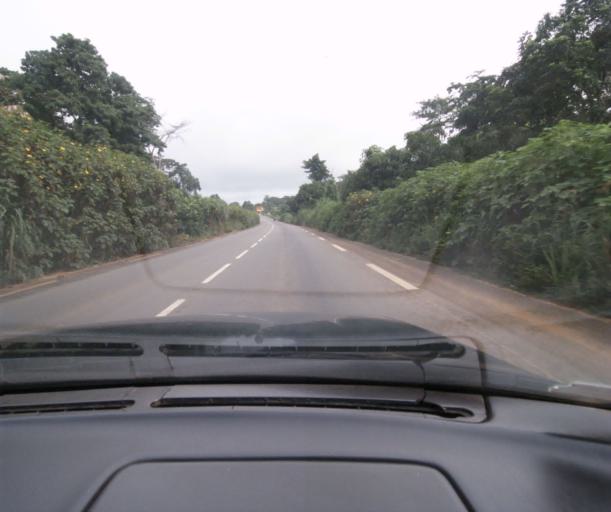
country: CM
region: Centre
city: Obala
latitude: 4.1606
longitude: 11.5057
